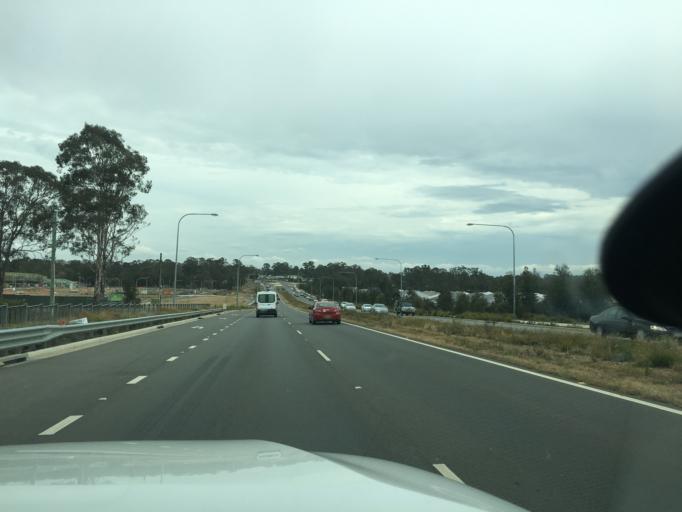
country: AU
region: New South Wales
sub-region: Campbelltown Municipality
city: Denham Court
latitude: -33.9586
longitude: 150.8246
